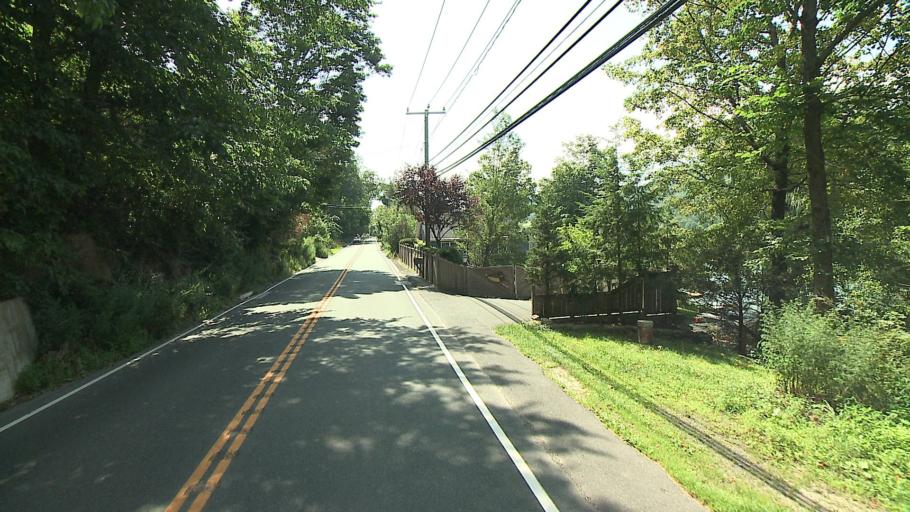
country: US
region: Connecticut
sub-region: Fairfield County
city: Sherman
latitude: 41.5215
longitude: -73.4793
